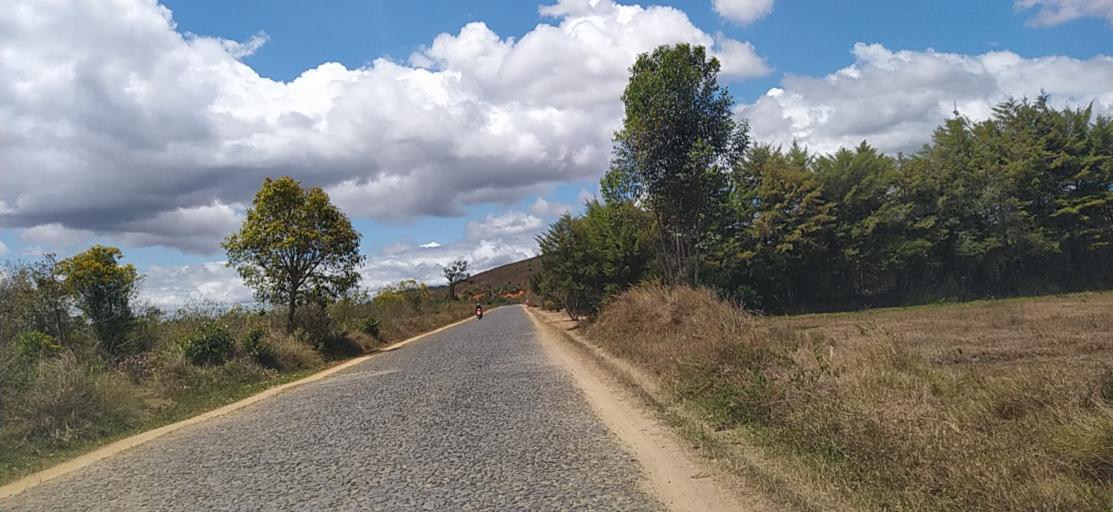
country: MG
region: Alaotra Mangoro
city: Moramanga
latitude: -18.7612
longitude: 48.2565
